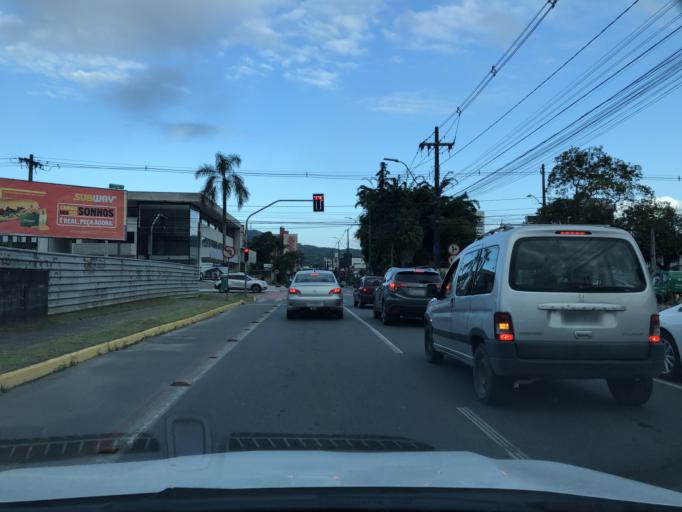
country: BR
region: Santa Catarina
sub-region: Joinville
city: Joinville
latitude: -26.2934
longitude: -48.8544
